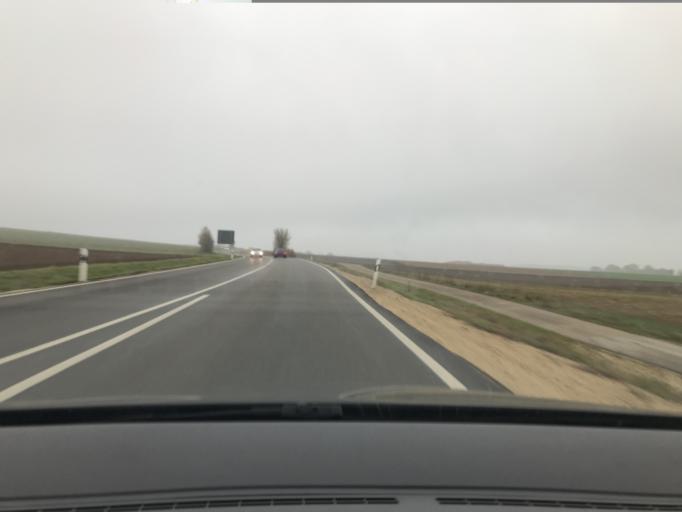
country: DE
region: Bavaria
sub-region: Swabia
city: Wallerstein
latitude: 48.9003
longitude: 10.4685
